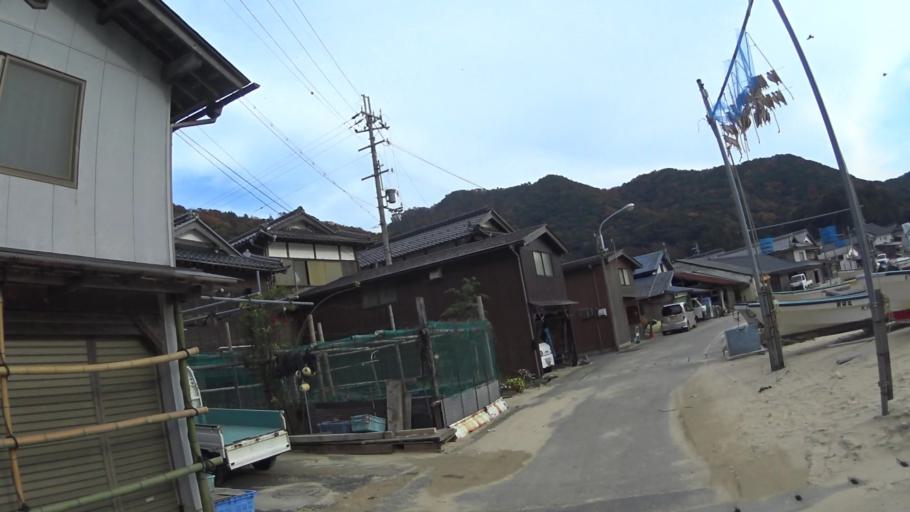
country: JP
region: Kyoto
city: Maizuru
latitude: 35.5709
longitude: 135.4272
